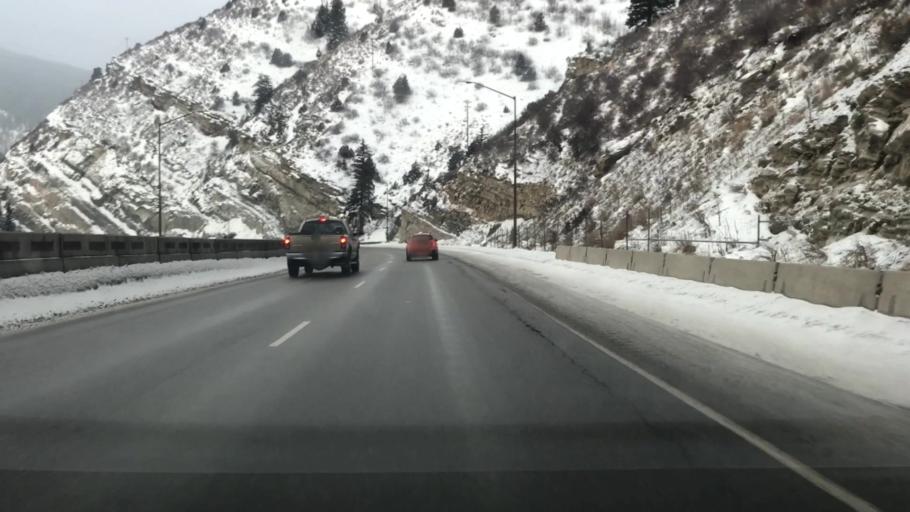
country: US
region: Colorado
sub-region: Eagle County
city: Minturn
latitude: 39.6153
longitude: -106.4403
